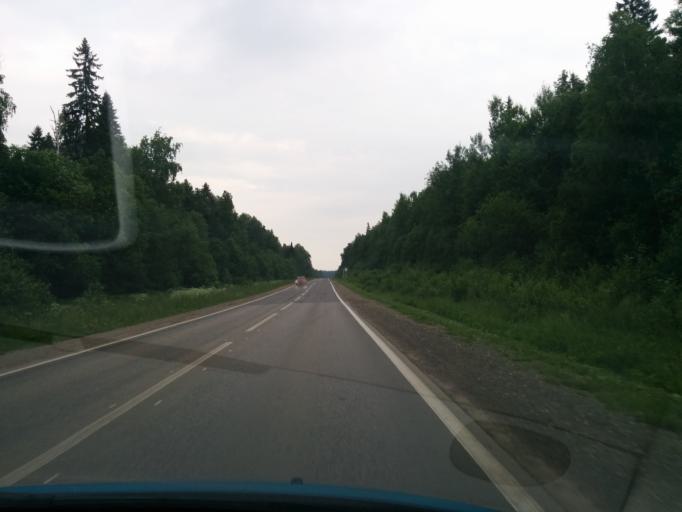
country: RU
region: Perm
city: Perm
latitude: 58.1838
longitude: 56.2219
